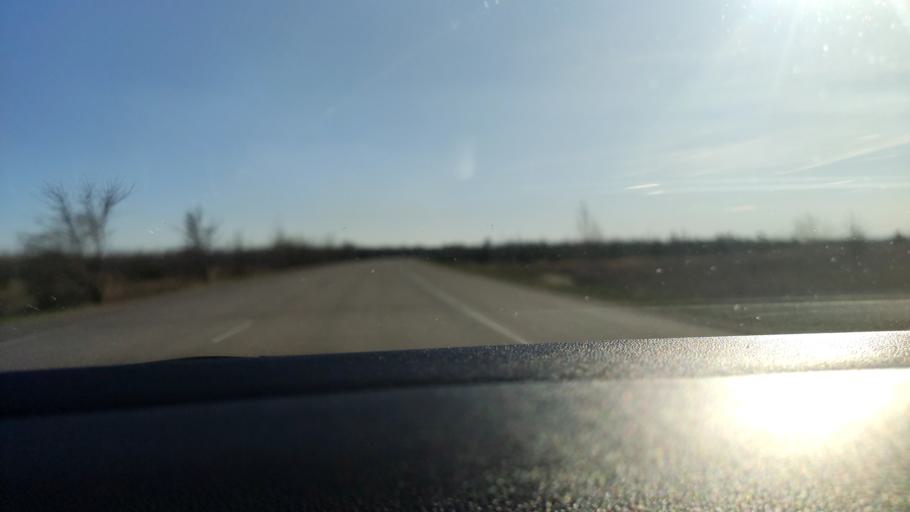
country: RU
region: Voronezj
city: Kolodeznyy
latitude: 51.3734
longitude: 39.2096
